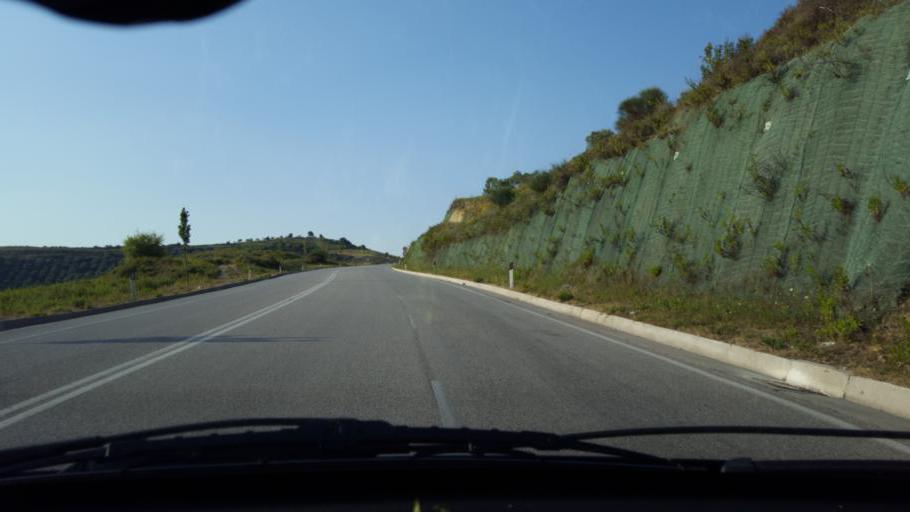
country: AL
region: Fier
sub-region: Rrethi i Mallakastres
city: Fratar
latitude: 40.4839
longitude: 19.8410
